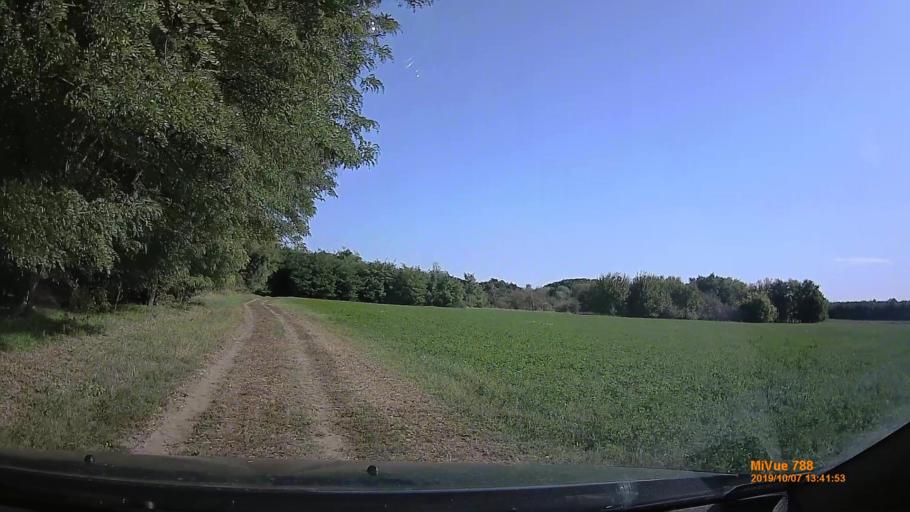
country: HU
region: Jasz-Nagykun-Szolnok
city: Cserkeszolo
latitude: 46.8821
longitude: 20.1933
